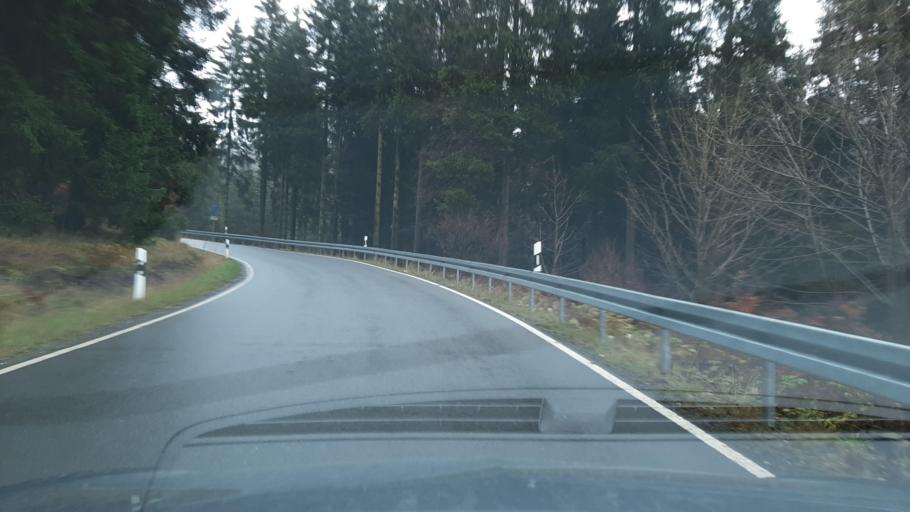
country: DE
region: North Rhine-Westphalia
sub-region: Regierungsbezirk Arnsberg
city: Winterberg
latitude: 51.2013
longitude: 8.4364
